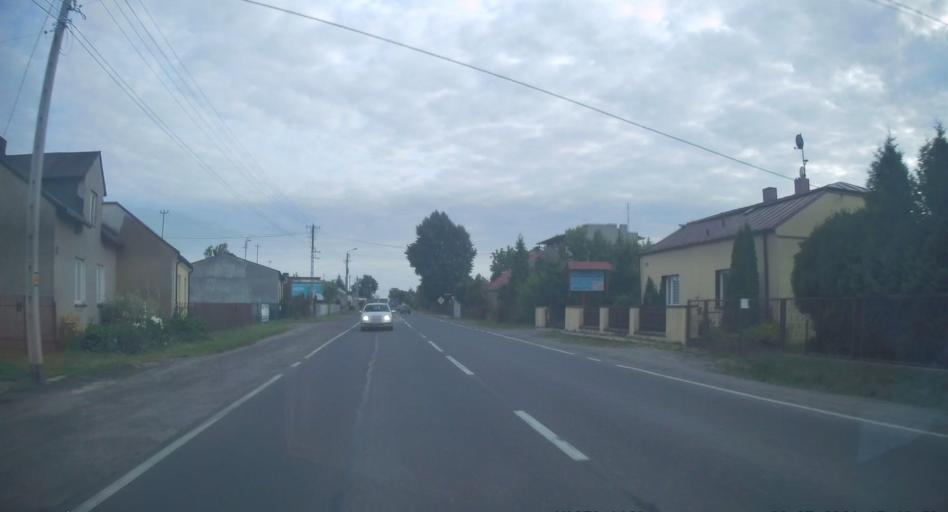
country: PL
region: Lodz Voivodeship
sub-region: Powiat radomszczanski
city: Radomsko
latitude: 51.0945
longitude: 19.4587
